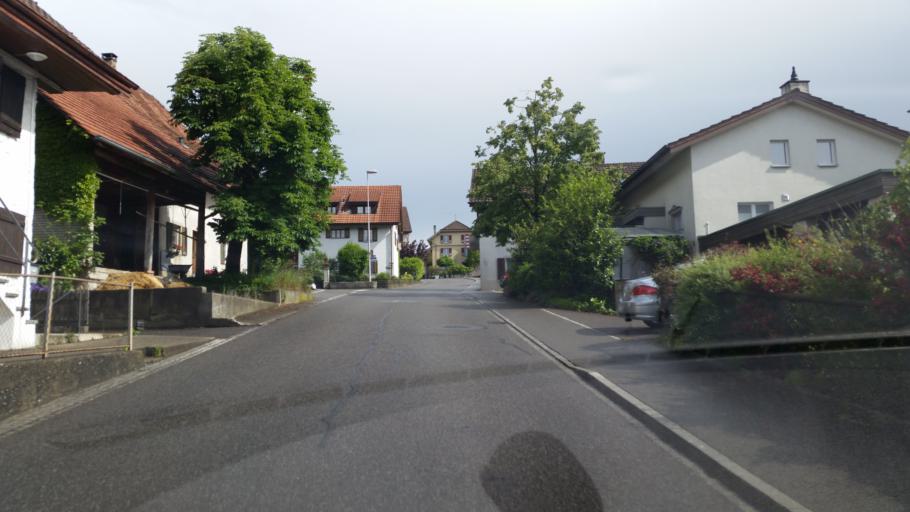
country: CH
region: Aargau
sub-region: Bezirk Lenzburg
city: Seengen
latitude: 47.3224
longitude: 8.2084
